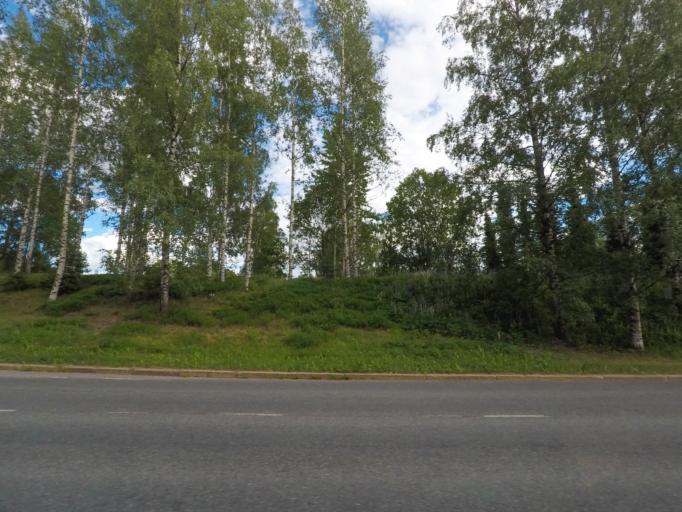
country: FI
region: Paijanne Tavastia
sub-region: Lahti
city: Lahti
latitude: 60.9735
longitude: 25.6352
